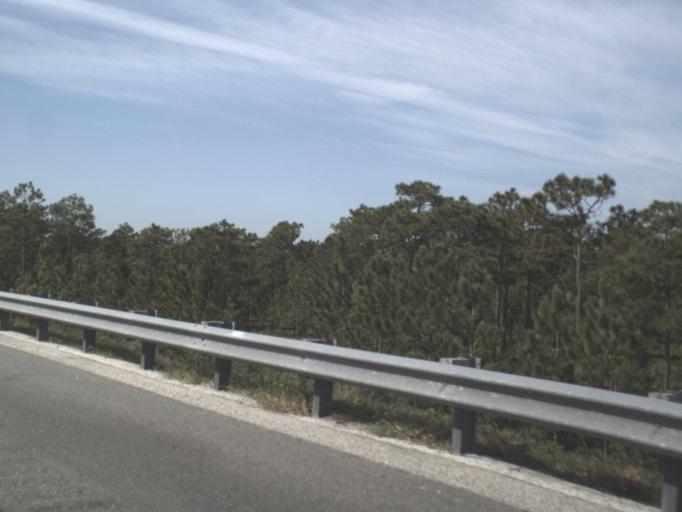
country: US
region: Florida
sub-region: Osceola County
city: Celebration
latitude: 28.3557
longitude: -81.4859
